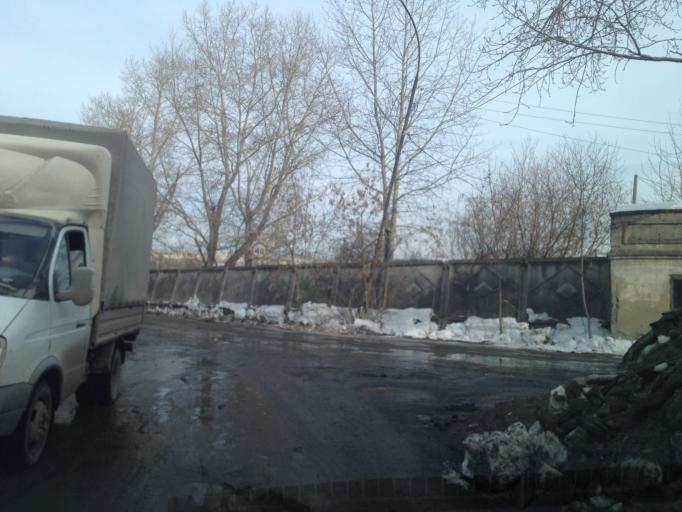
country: RU
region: Sverdlovsk
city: Yekaterinburg
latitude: 56.8182
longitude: 60.6598
